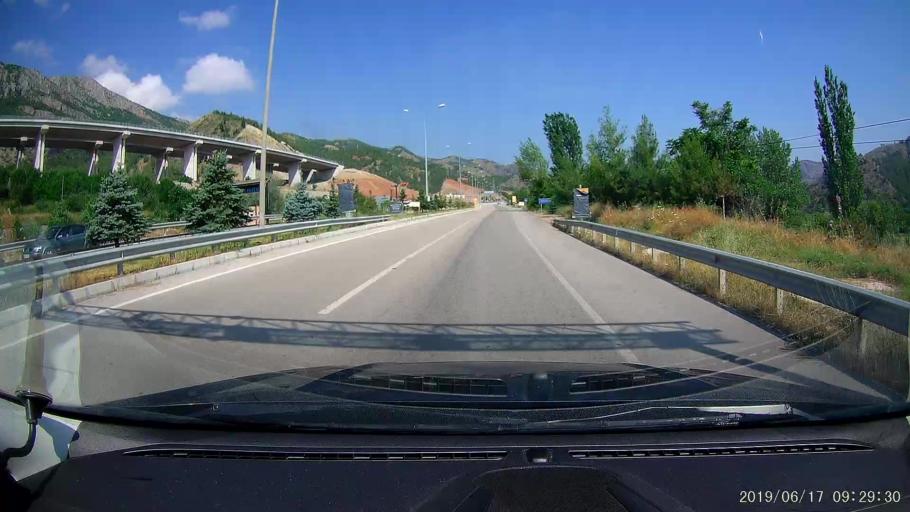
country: TR
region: Amasya
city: Amasya
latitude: 40.6970
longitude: 35.8114
